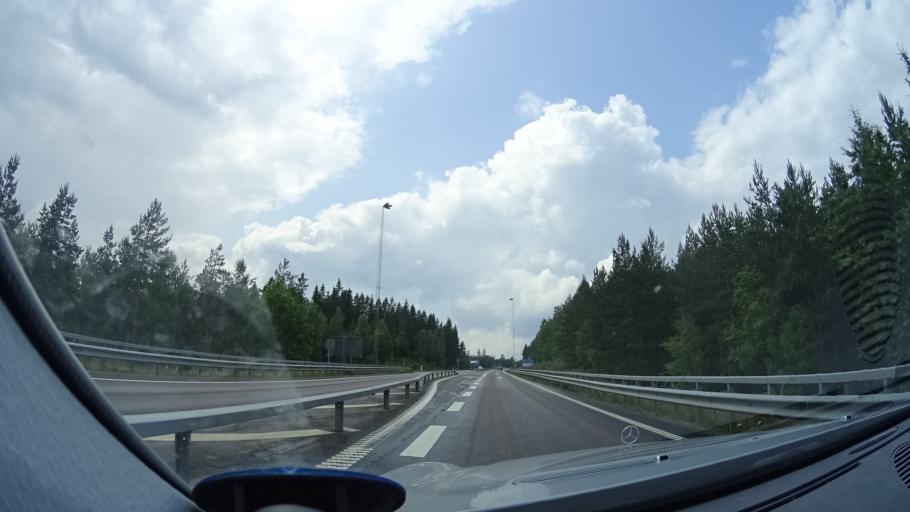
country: SE
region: Kalmar
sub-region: Nybro Kommun
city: Nybro
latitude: 56.7072
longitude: 15.7476
